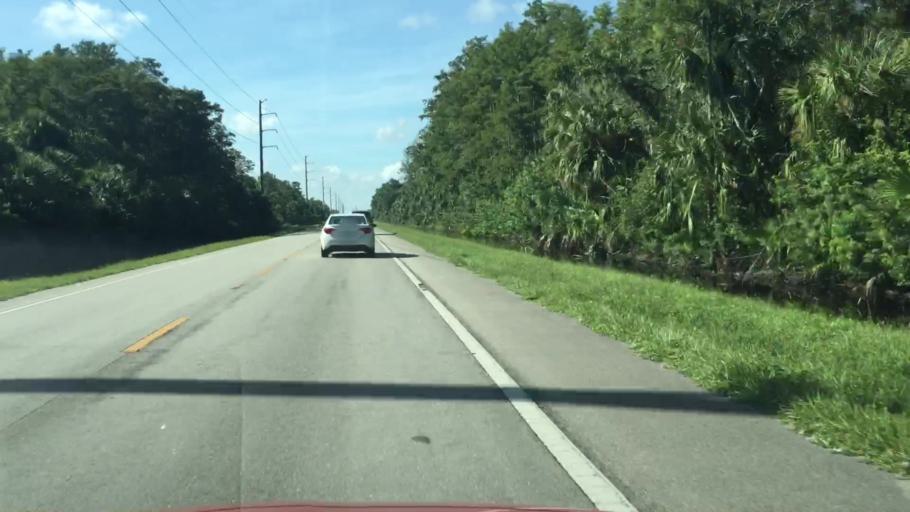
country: US
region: Florida
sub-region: Collier County
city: Orangetree
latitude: 26.3352
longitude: -81.5950
